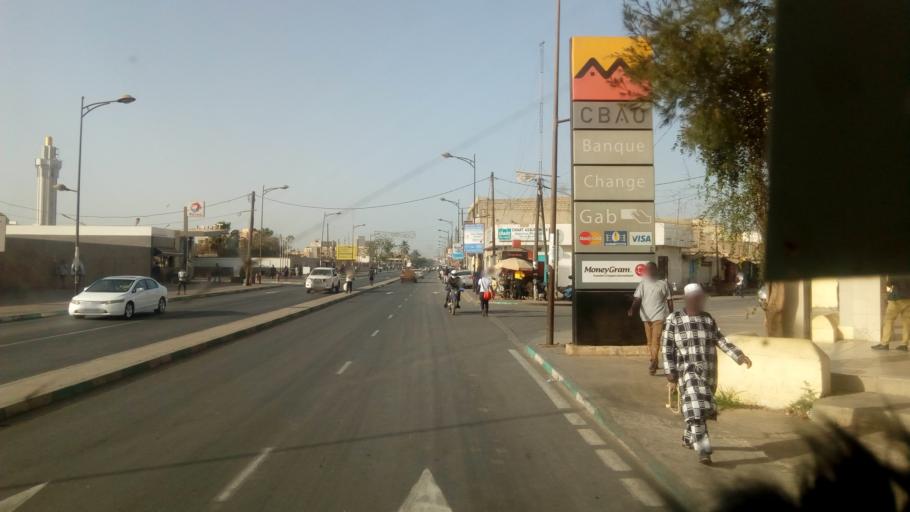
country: SN
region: Dakar
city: Dakar
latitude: 14.6991
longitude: -17.4472
